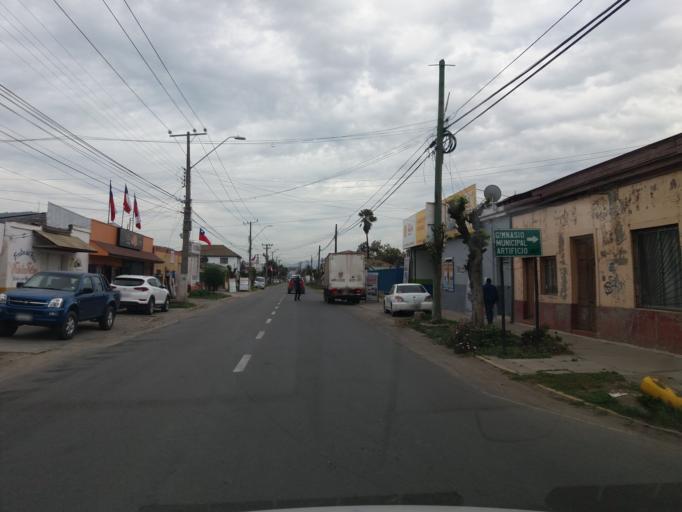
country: CL
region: Valparaiso
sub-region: Provincia de Quillota
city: Hacienda La Calera
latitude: -32.7748
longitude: -71.1920
